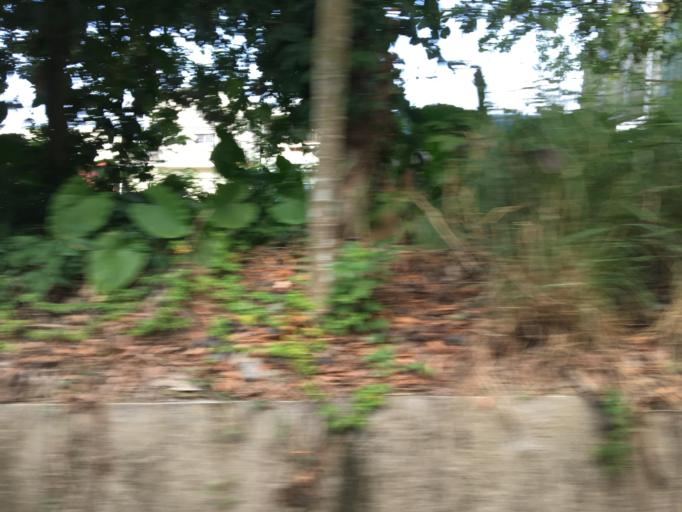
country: TW
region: Taiwan
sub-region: Chiayi
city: Jiayi Shi
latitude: 23.4927
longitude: 120.5013
